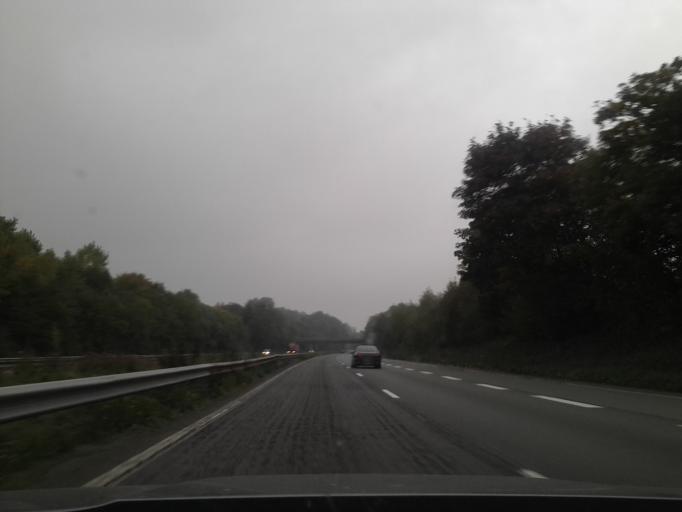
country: FR
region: Nord-Pas-de-Calais
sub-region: Departement du Nord
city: Saultain
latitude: 50.3437
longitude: 3.5700
